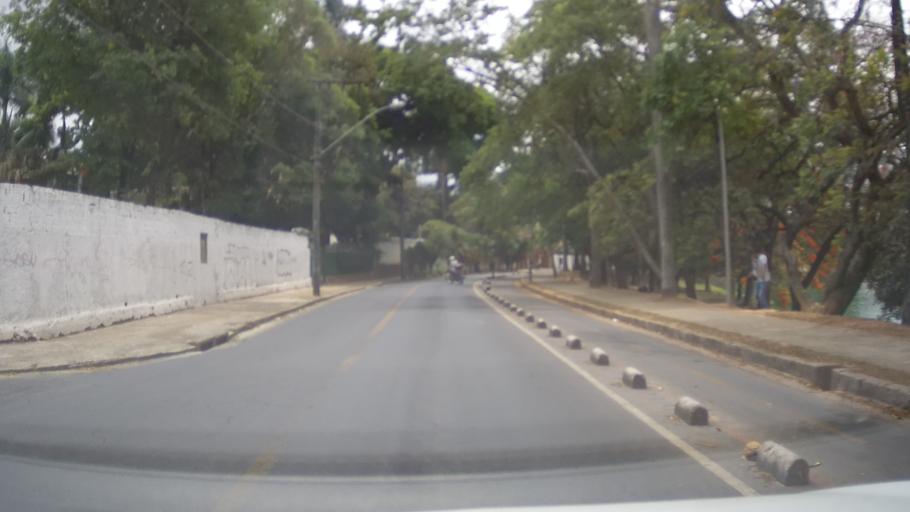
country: BR
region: Minas Gerais
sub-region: Belo Horizonte
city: Belo Horizonte
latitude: -19.8489
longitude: -43.9720
